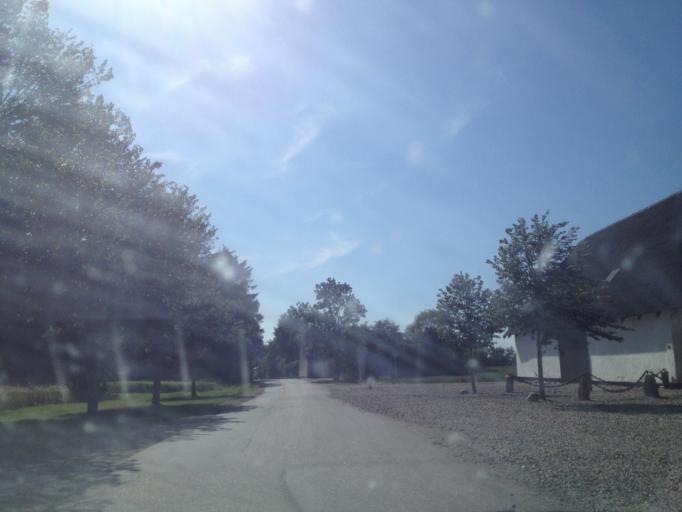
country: DK
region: South Denmark
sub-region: Kolding Kommune
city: Christiansfeld
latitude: 55.4073
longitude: 9.5021
